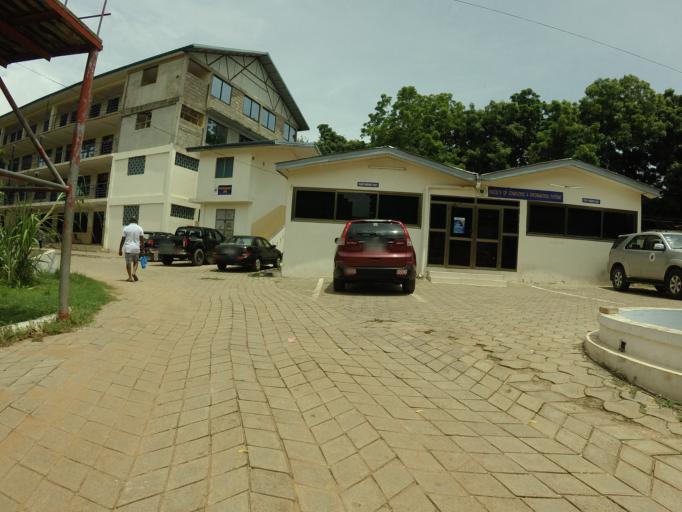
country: GH
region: Greater Accra
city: Accra
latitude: 5.5959
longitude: -0.2239
